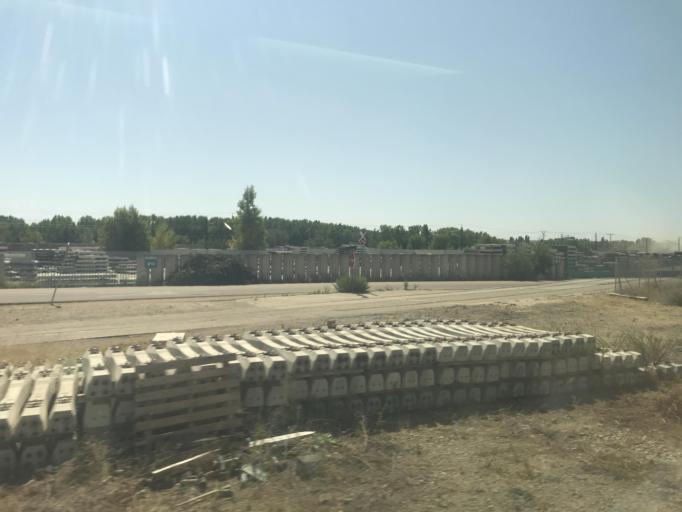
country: ES
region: Castille and Leon
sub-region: Provincia de Palencia
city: Venta de Banos
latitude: 41.9117
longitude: -4.5030
